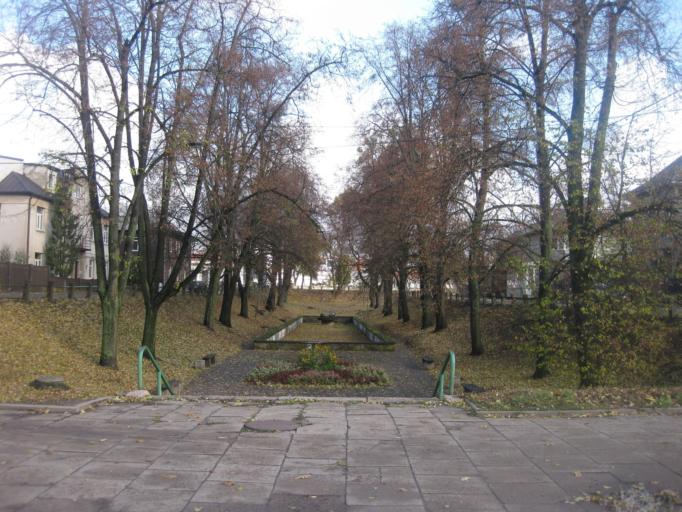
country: LT
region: Kauno apskritis
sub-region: Kaunas
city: Kaunas
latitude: 54.9013
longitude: 23.9258
